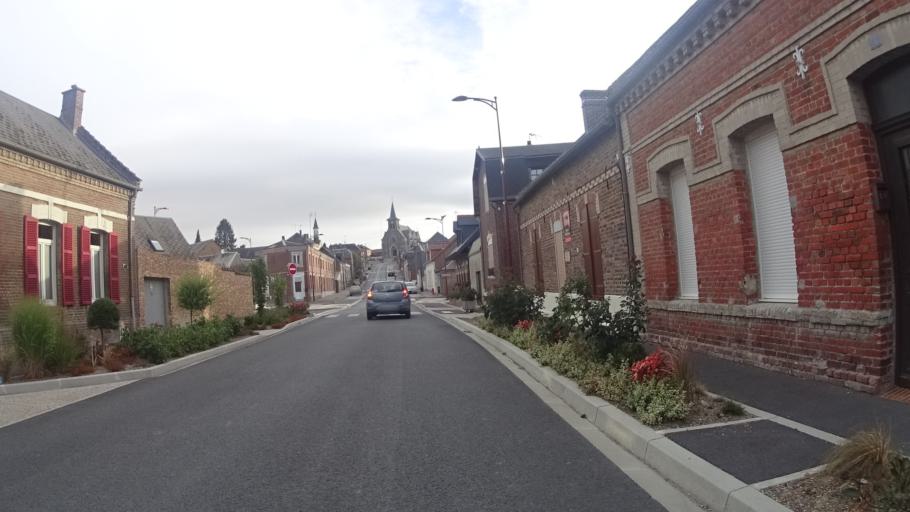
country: FR
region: Picardie
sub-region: Departement de l'Aisne
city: Origny-Sainte-Benoite
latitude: 49.8297
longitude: 3.4675
